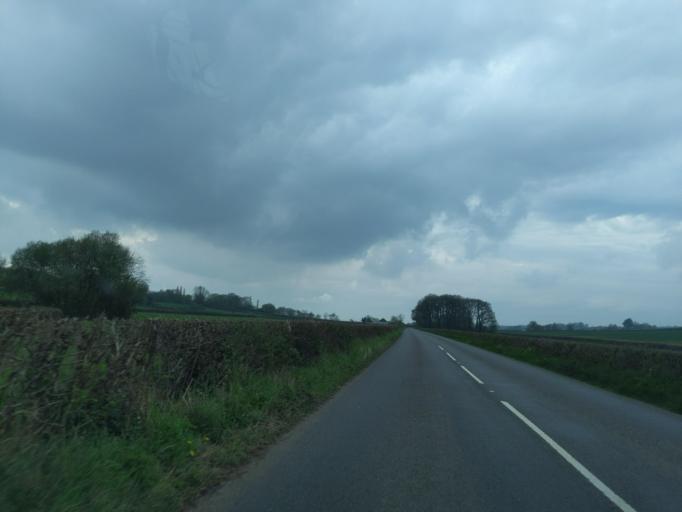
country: GB
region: England
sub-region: Devon
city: Winkleigh
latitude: 50.8458
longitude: -3.8527
